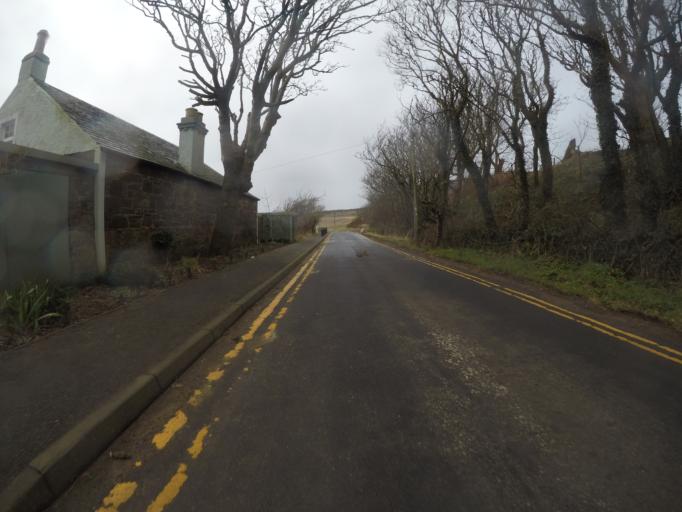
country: GB
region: Scotland
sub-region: North Ayrshire
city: West Kilbride
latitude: 55.6975
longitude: -4.8908
